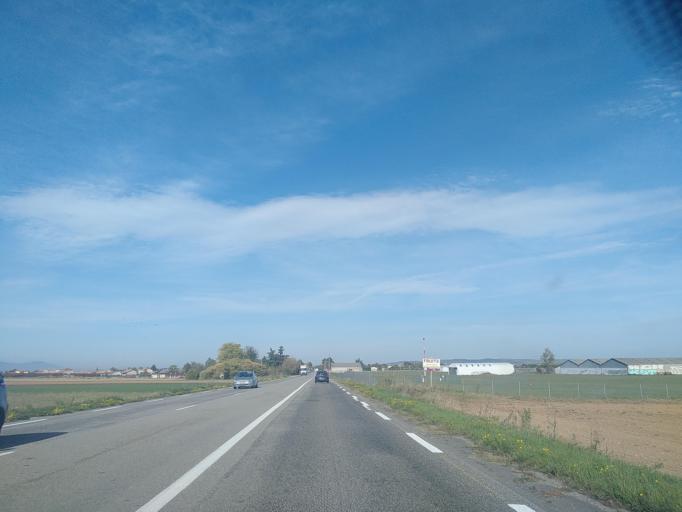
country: FR
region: Rhone-Alpes
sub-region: Departement de la Drome
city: Andancette
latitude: 45.2512
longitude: 4.8219
